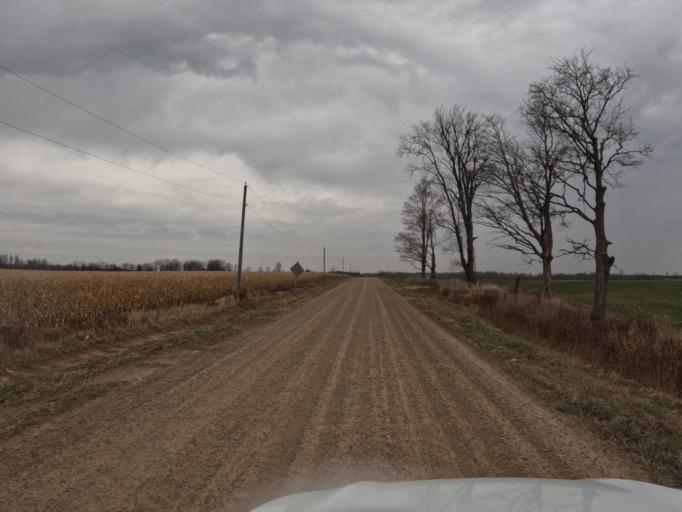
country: CA
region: Ontario
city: Shelburne
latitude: 43.8863
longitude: -80.3822
